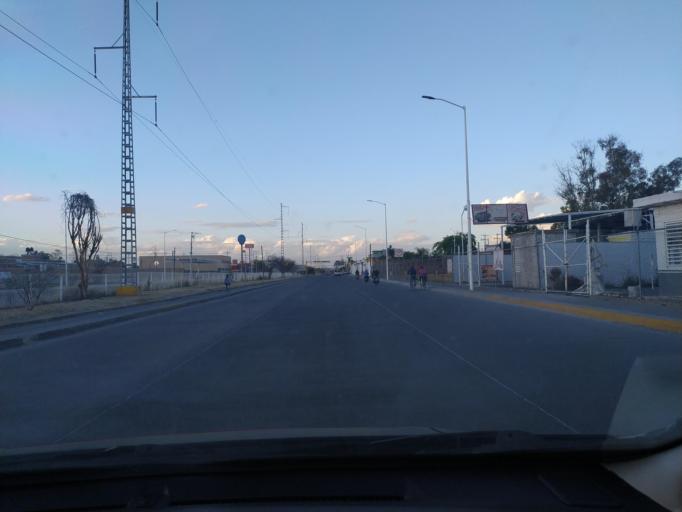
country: LA
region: Oudomxai
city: Muang La
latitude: 21.0151
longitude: 101.8697
